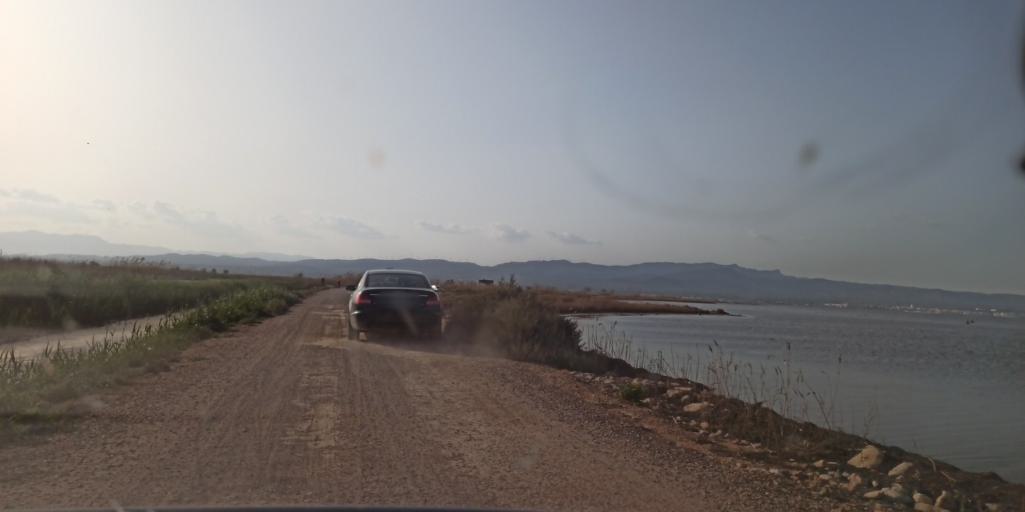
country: ES
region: Catalonia
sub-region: Provincia de Tarragona
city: L'Ampolla
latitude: 40.7692
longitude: 0.7308
